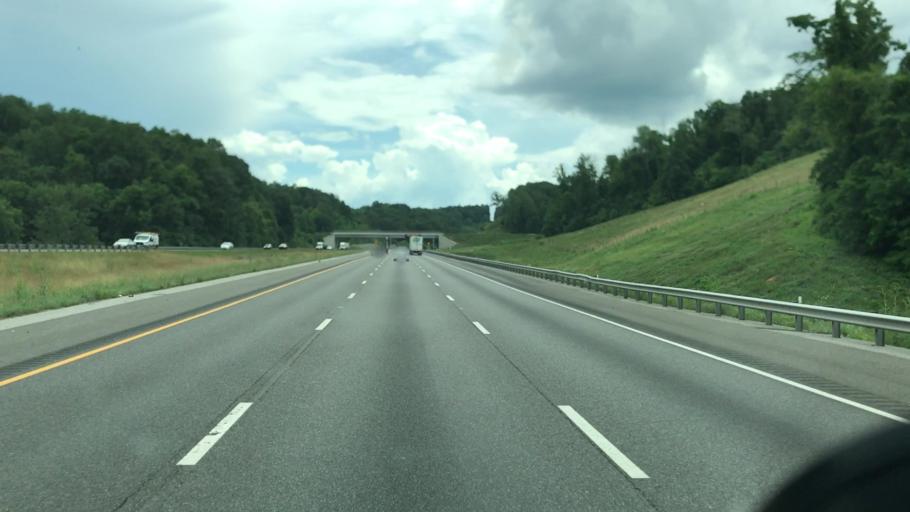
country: US
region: Virginia
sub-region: Montgomery County
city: Shawsville
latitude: 37.1788
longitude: -80.2987
